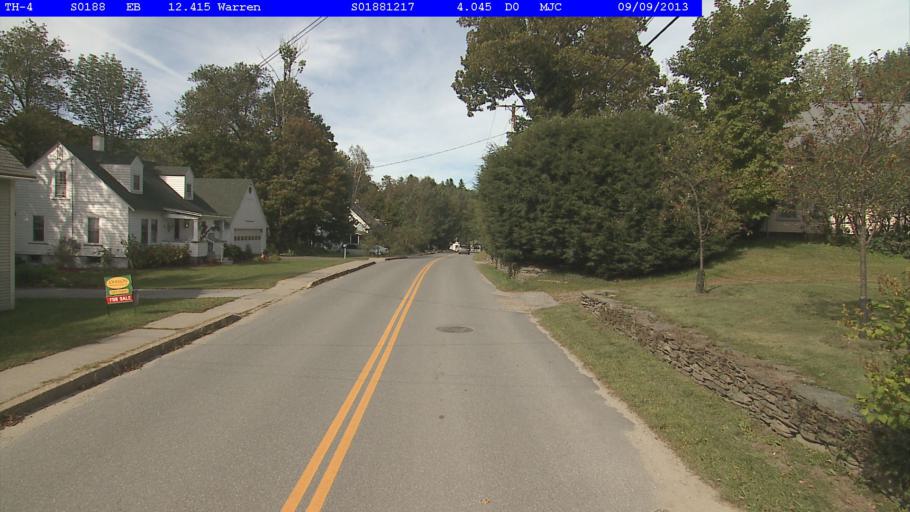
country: US
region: Vermont
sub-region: Washington County
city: Northfield
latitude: 44.1122
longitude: -72.8562
